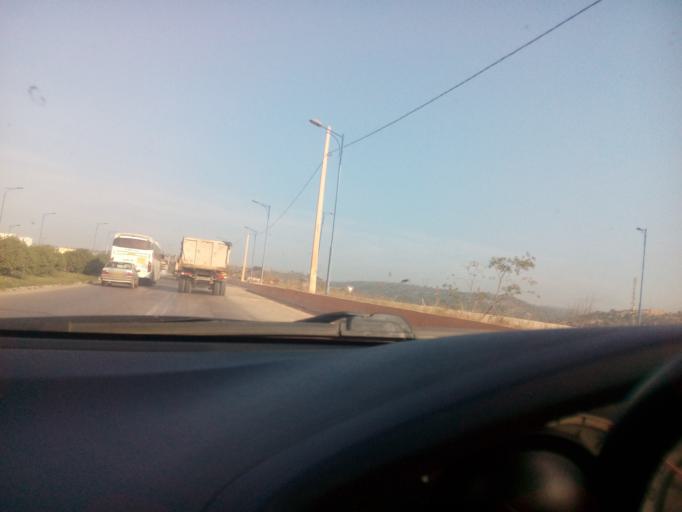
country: DZ
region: Oran
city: Es Senia
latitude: 35.6261
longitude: -0.7187
